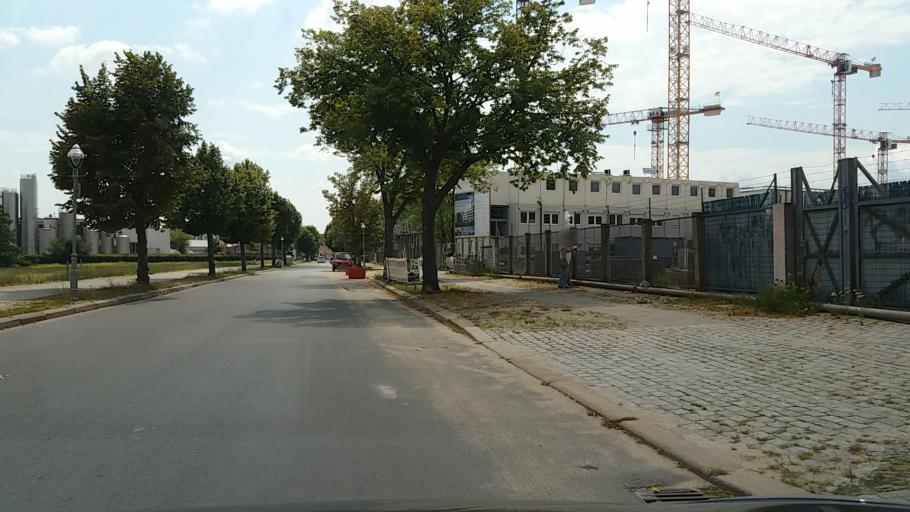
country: DE
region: Berlin
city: Hakenfelde
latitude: 52.5641
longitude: 13.2153
